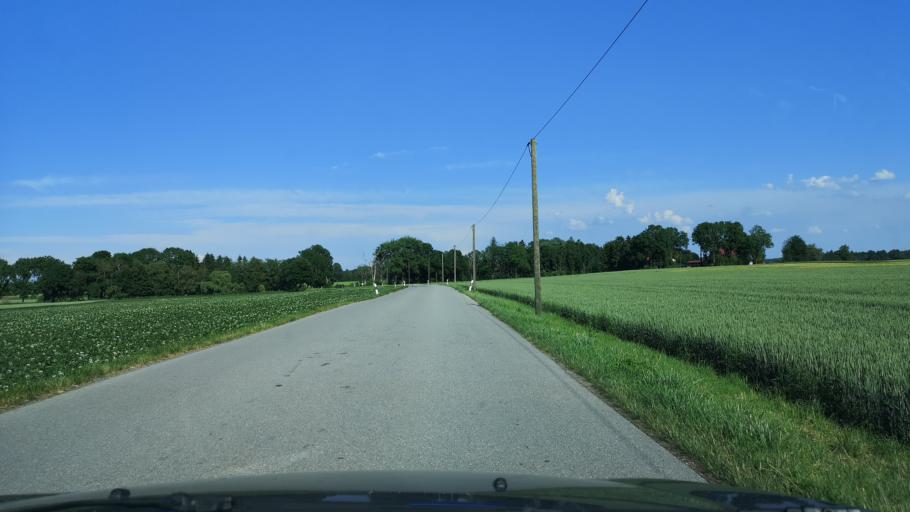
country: DE
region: Bavaria
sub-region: Upper Bavaria
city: Eichenried
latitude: 48.2662
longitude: 11.7418
